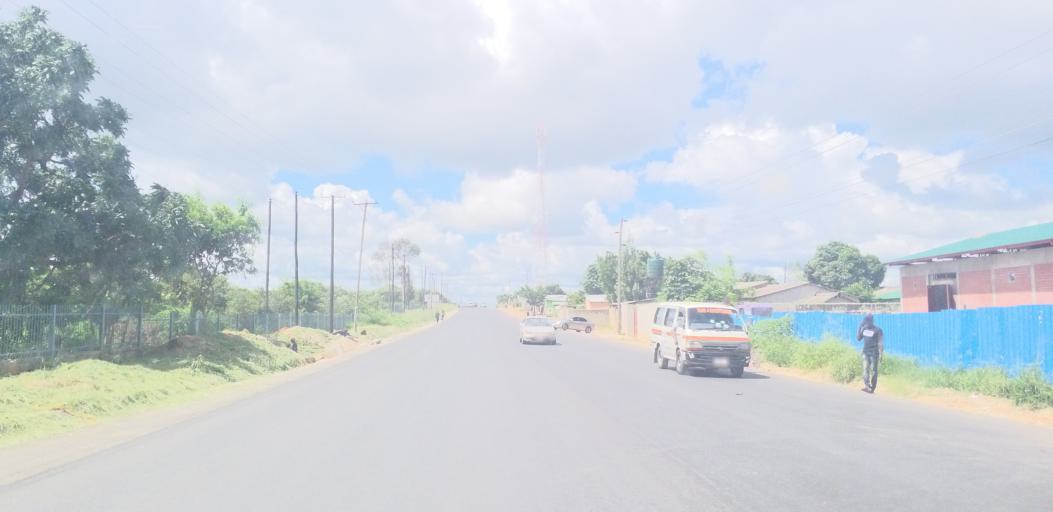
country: ZM
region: Lusaka
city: Lusaka
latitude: -15.3617
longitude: 28.3217
